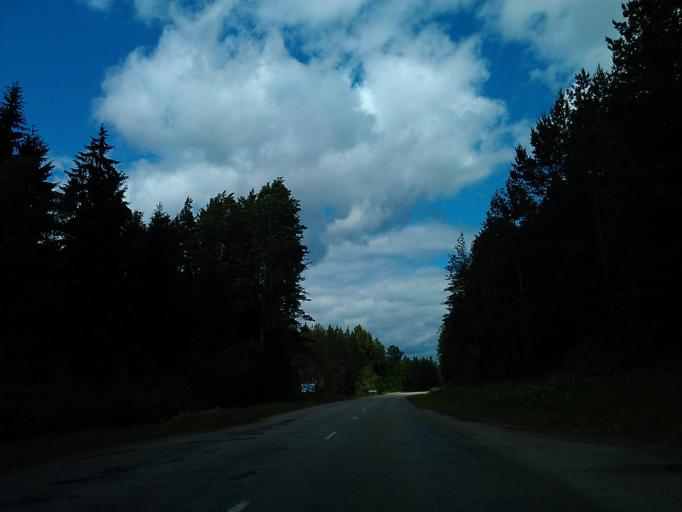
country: LV
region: Talsu Rajons
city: Sabile
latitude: 57.0700
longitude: 22.5367
